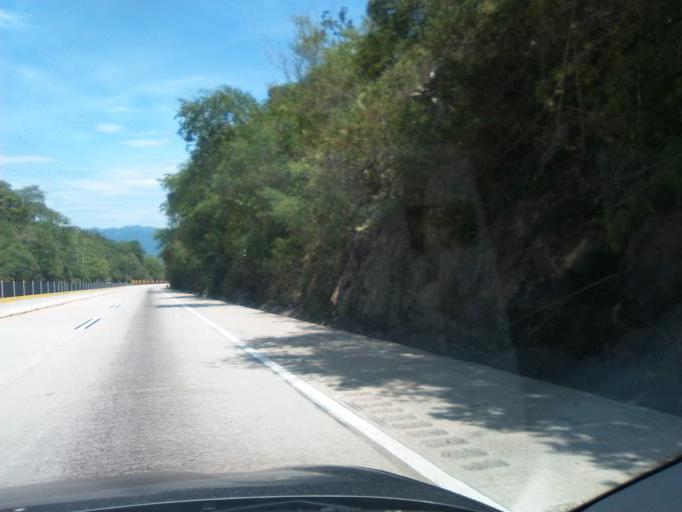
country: MX
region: Guerrero
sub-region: Acapulco de Juarez
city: Kilometro 30
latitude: 16.9558
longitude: -99.7492
